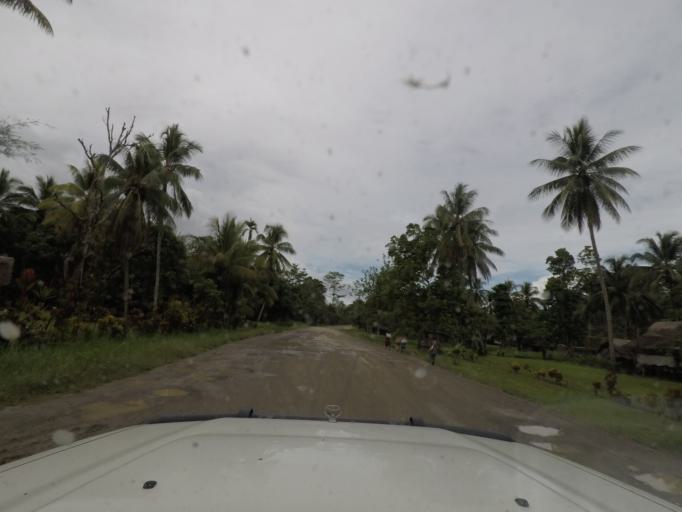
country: PG
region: Eastern Highlands
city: Goroka
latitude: -5.6510
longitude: 145.4932
